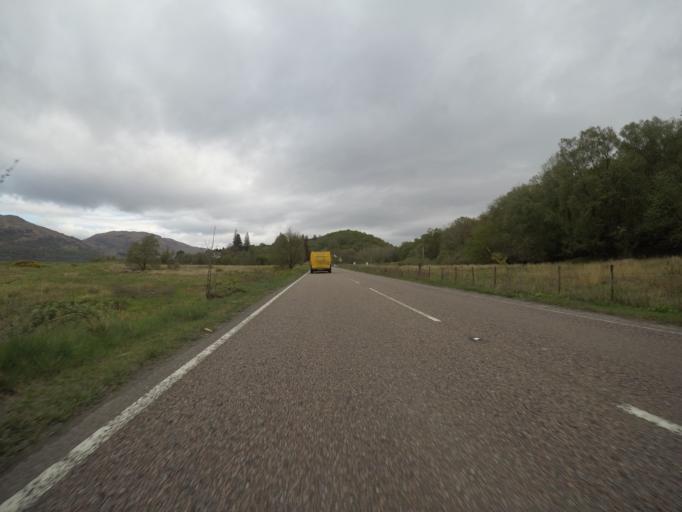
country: GB
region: Scotland
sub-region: Highland
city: Fort William
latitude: 56.7710
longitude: -5.1692
